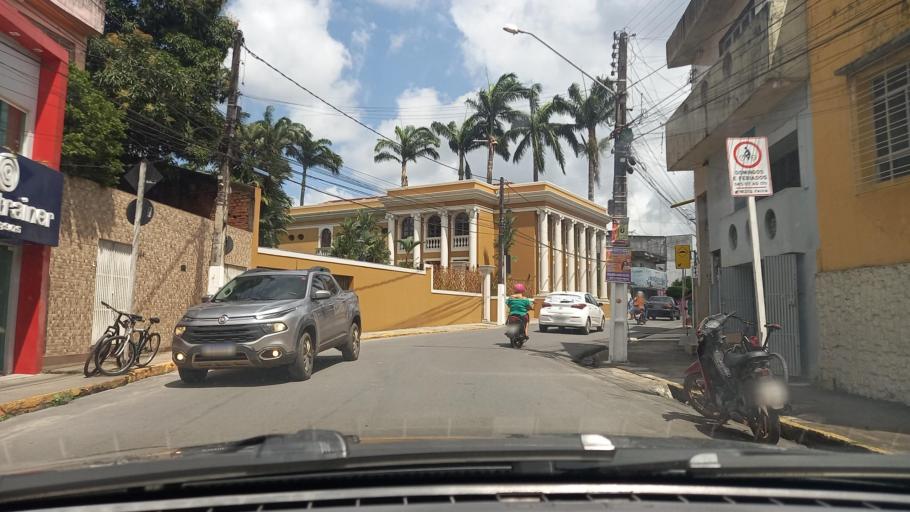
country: BR
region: Pernambuco
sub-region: Goiana
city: Goiana
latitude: -7.5575
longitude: -35.0017
